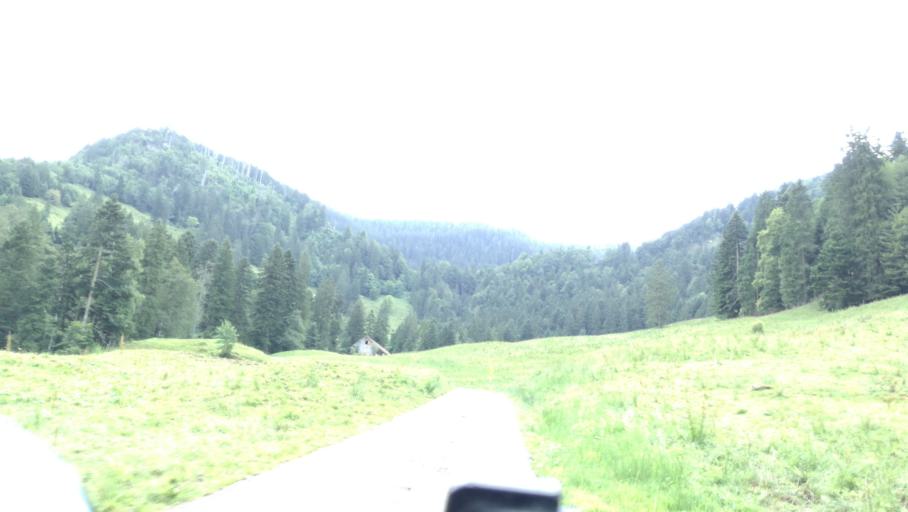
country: CH
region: Zug
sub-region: Zug
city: Unterageri
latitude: 47.0941
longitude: 8.5661
